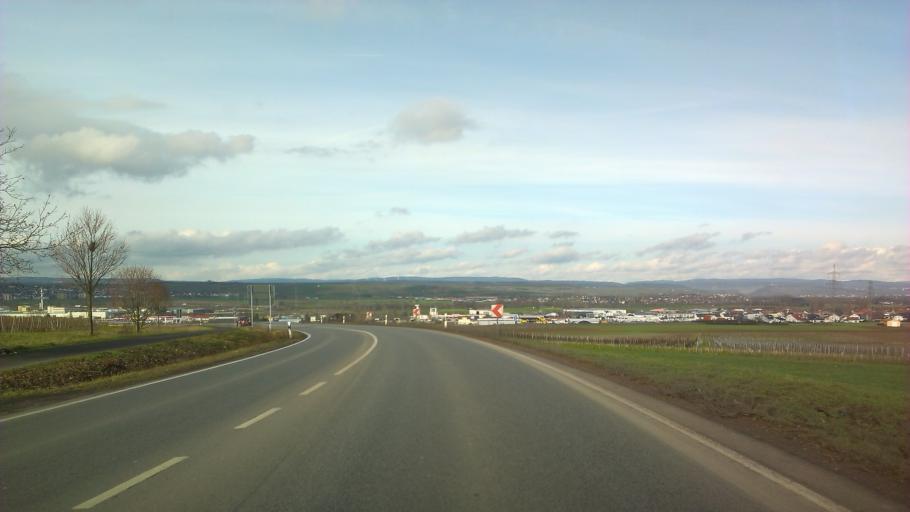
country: DE
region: Rheinland-Pfalz
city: Bretzenheim
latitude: 49.8488
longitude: 7.9072
